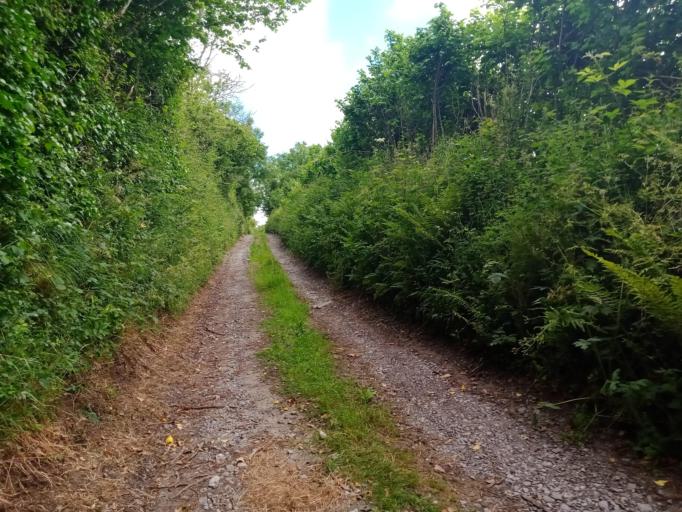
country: IE
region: Leinster
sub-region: Kilkenny
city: Ballyragget
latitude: 52.7773
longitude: -7.4648
